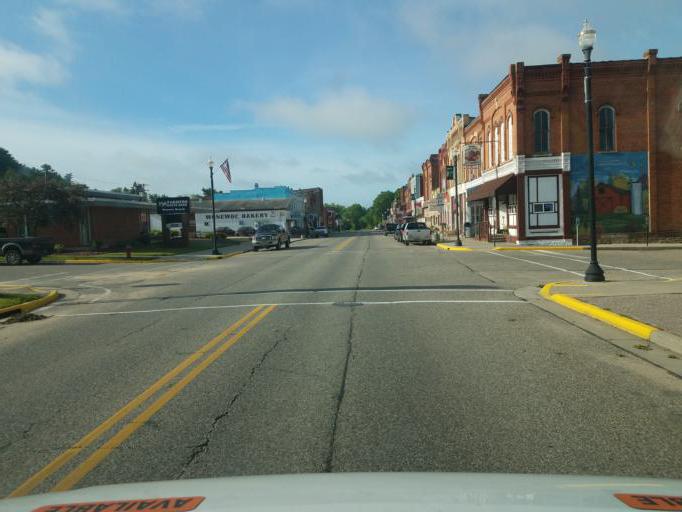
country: US
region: Wisconsin
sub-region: Juneau County
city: Elroy
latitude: 43.6545
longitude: -90.2234
